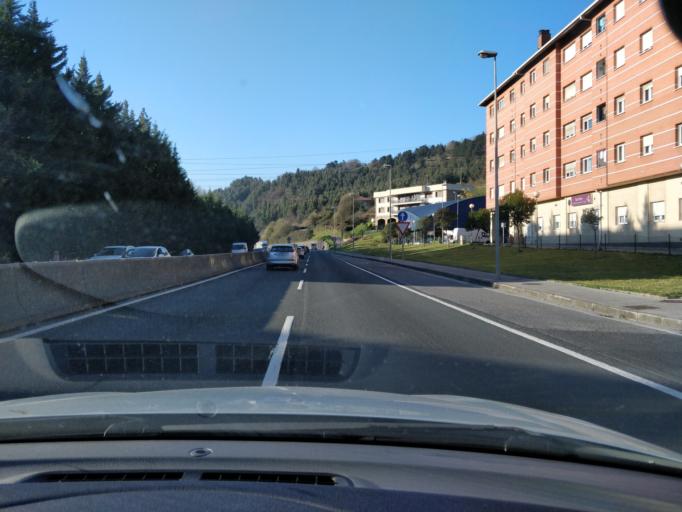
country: ES
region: Basque Country
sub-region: Bizkaia
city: Basauri
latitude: 43.2415
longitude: -2.8749
